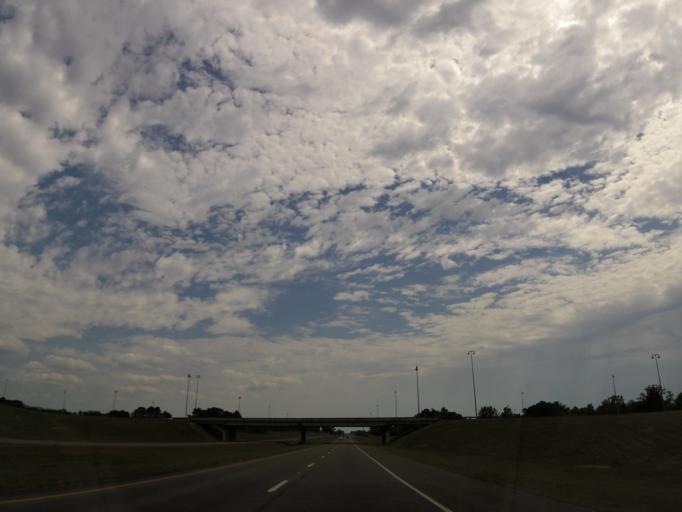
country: US
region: Alabama
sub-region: Jackson County
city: Stevenson
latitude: 34.8557
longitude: -85.8223
